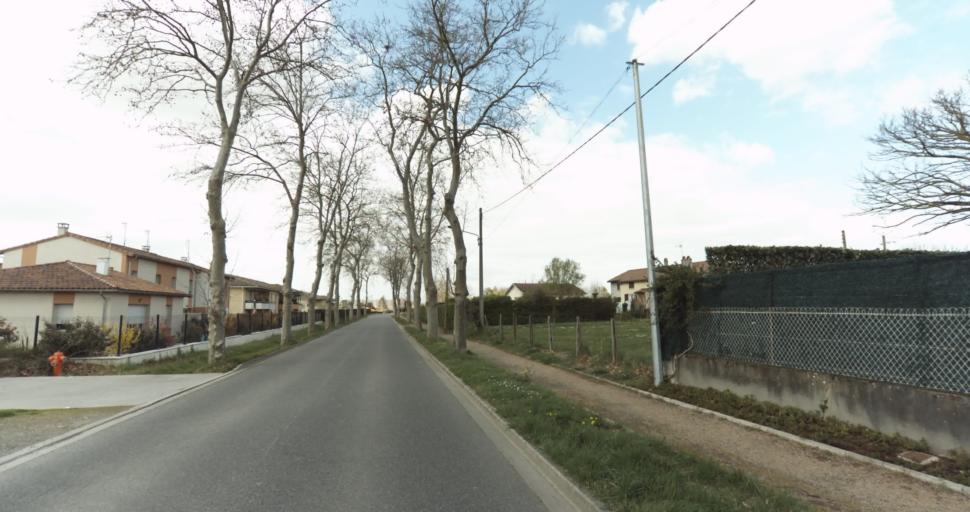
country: FR
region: Midi-Pyrenees
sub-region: Departement de la Haute-Garonne
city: Auterive
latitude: 43.3563
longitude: 1.4778
